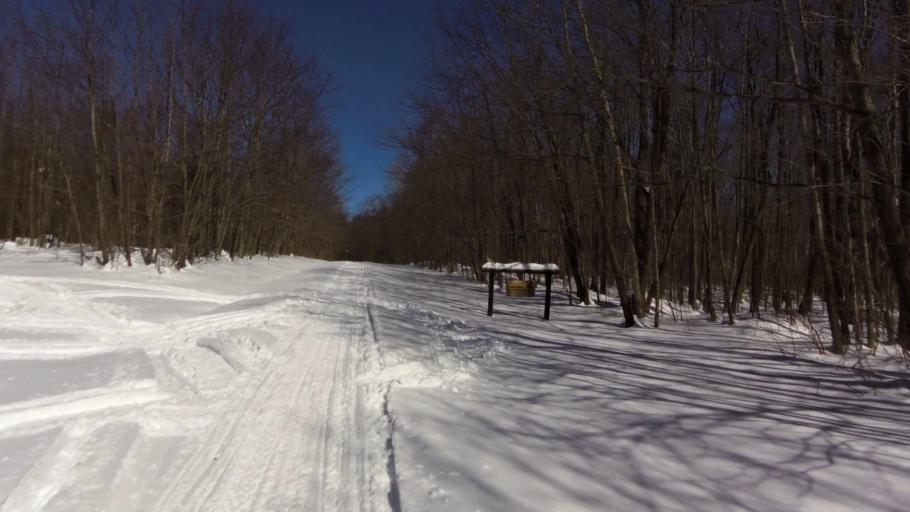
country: US
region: New York
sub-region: Allegany County
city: Cuba
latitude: 42.3198
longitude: -78.2311
